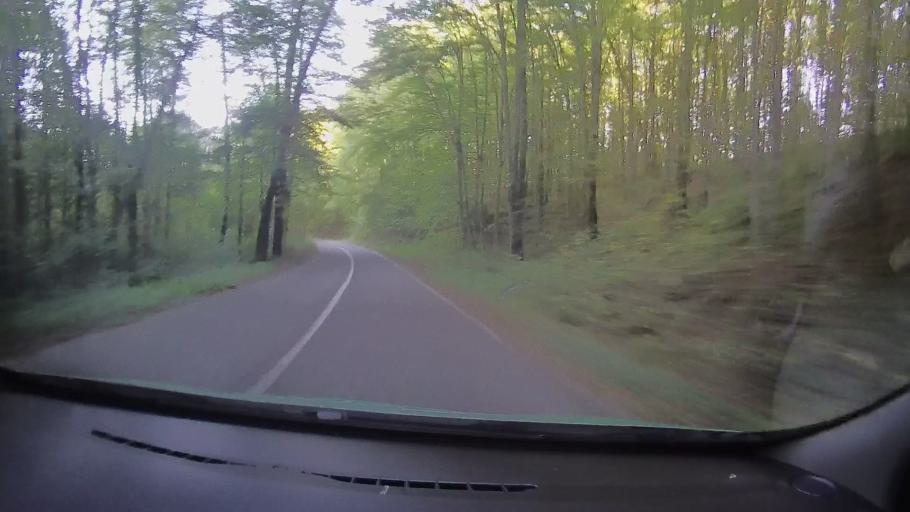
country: RO
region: Timis
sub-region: Comuna Nadrag
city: Nadrag
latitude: 45.6860
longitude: 22.1588
